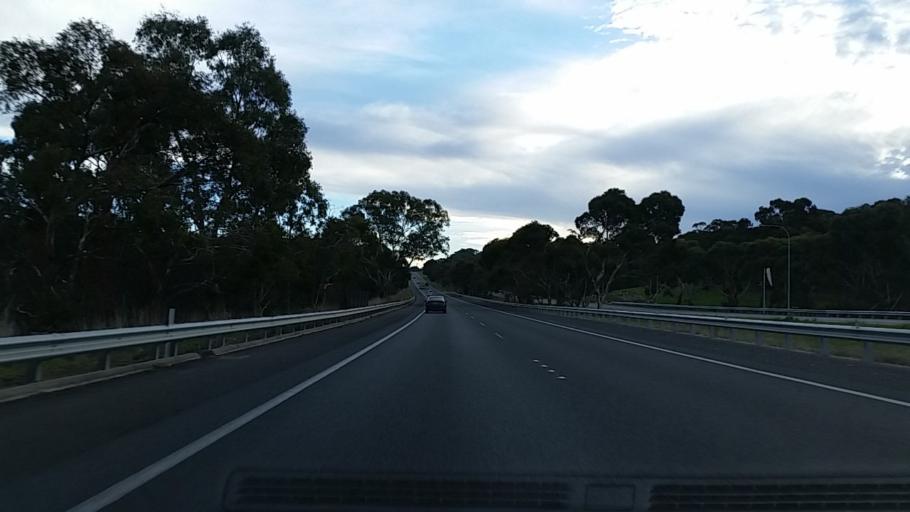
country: AU
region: South Australia
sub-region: Mount Barker
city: Nairne
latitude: -35.0541
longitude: 138.8932
